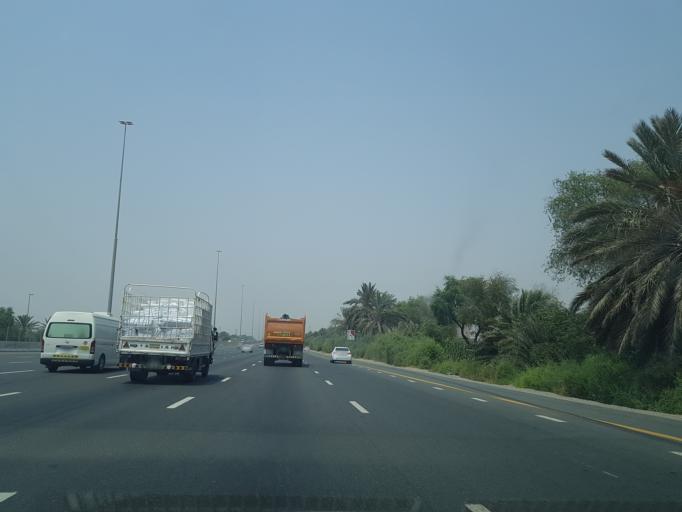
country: AE
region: Ash Shariqah
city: Sharjah
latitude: 25.1424
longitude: 55.3838
